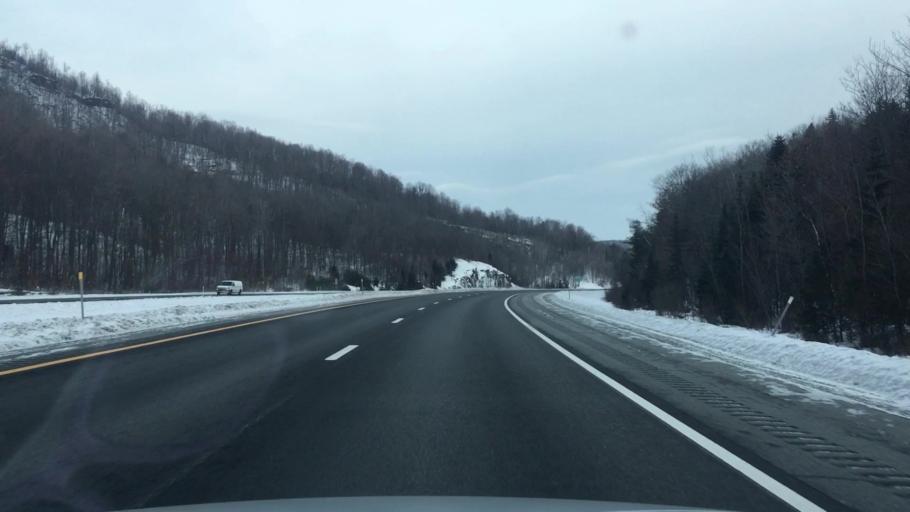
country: US
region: New Hampshire
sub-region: Grafton County
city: Enfield
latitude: 43.5745
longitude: -72.1594
